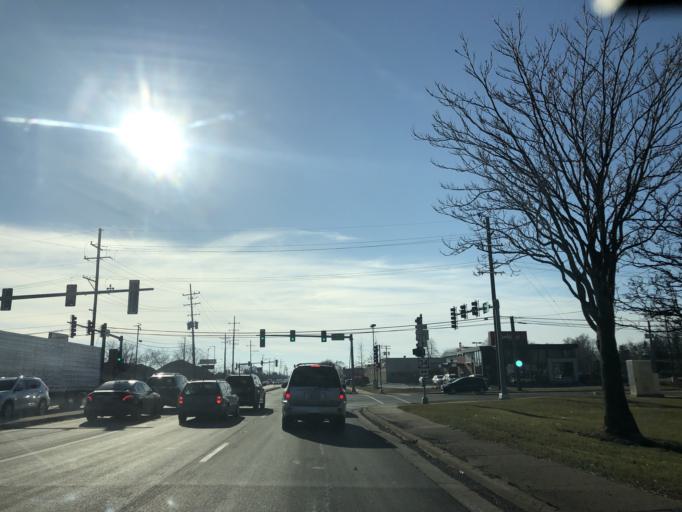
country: US
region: Illinois
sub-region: Cook County
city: Lyons
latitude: 41.8167
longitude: -87.8340
